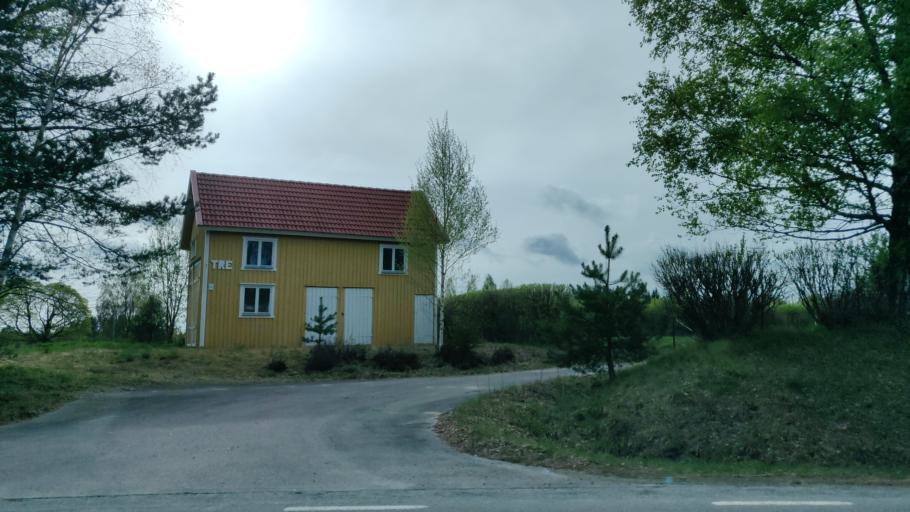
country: SE
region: Vaermland
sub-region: Munkfors Kommun
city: Munkfors
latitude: 59.7986
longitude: 13.5037
